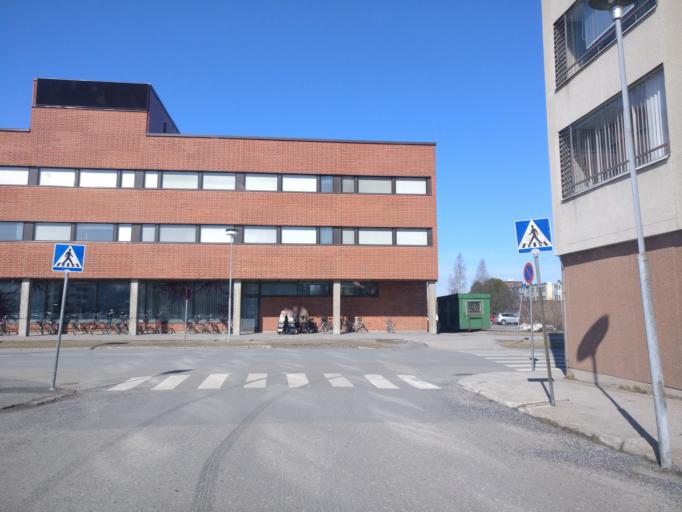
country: FI
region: Lapland
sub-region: Kemi-Tornio
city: Kemi
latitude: 65.7355
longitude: 24.5593
